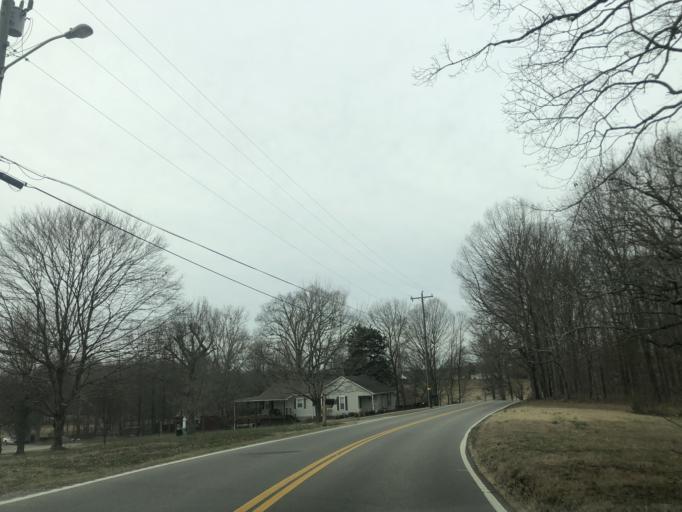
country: US
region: Tennessee
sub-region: Robertson County
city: Ridgetop
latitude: 36.3951
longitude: -86.7816
